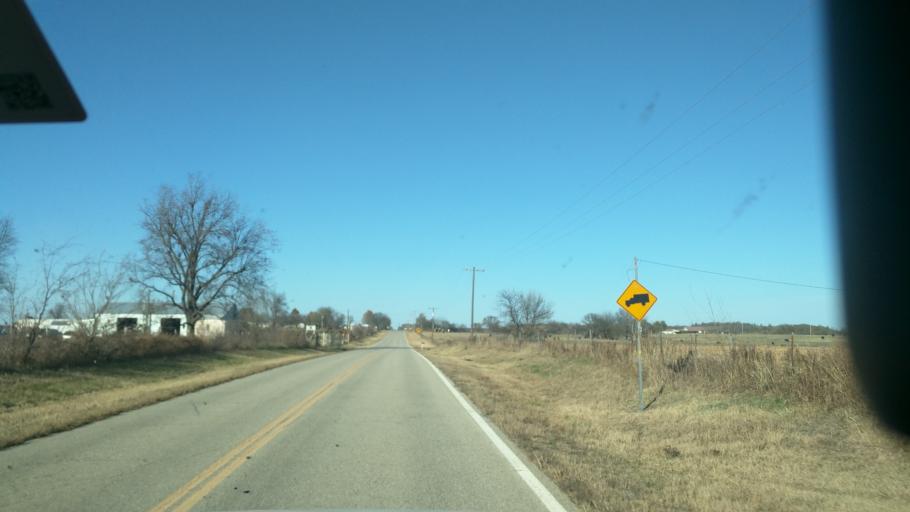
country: US
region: Oklahoma
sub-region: Nowata County
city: Nowata
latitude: 36.7670
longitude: -95.5396
